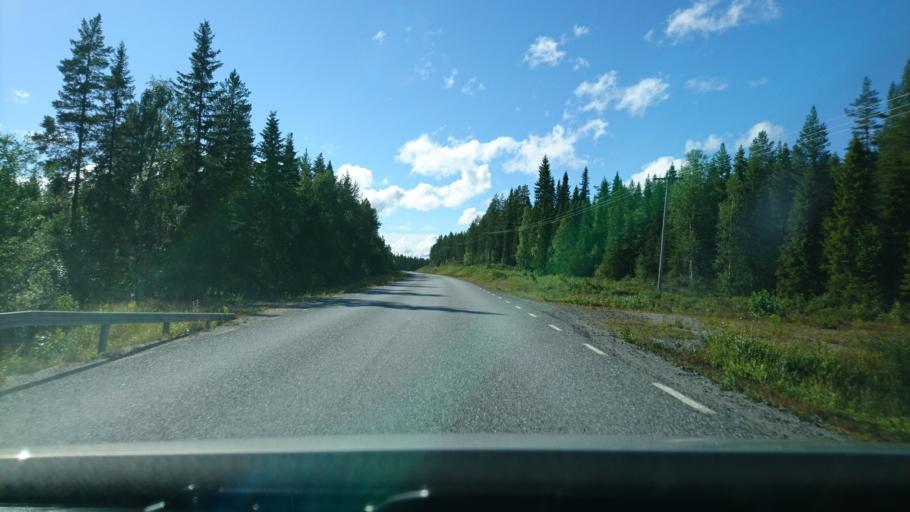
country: SE
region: Vaesterbotten
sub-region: Vilhelmina Kommun
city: Vilhelmina
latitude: 64.3661
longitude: 16.9422
